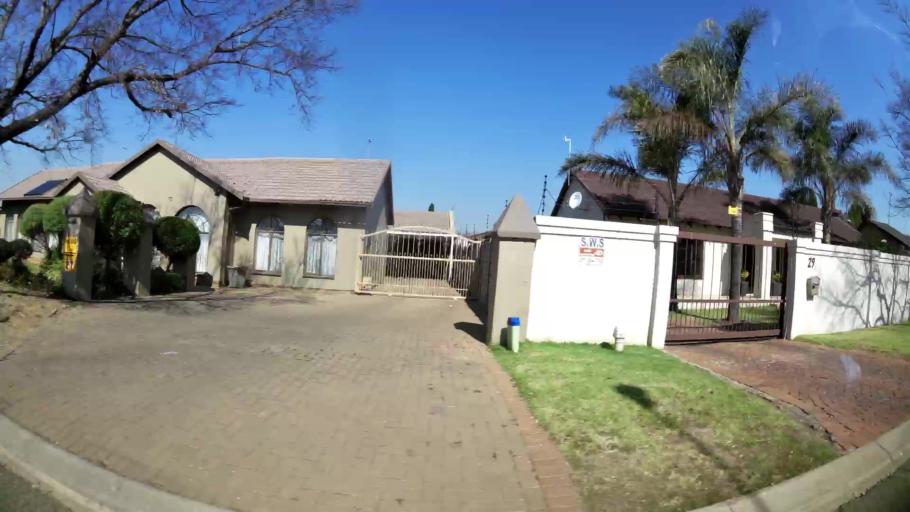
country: ZA
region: Gauteng
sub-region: Ekurhuleni Metropolitan Municipality
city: Boksburg
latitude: -26.1721
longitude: 28.2668
